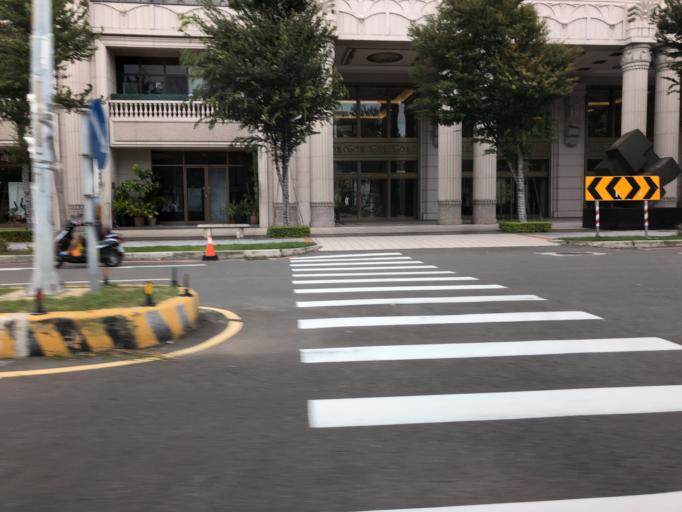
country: TW
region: Taiwan
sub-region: Hsinchu
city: Zhubei
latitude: 24.8163
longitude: 121.0201
